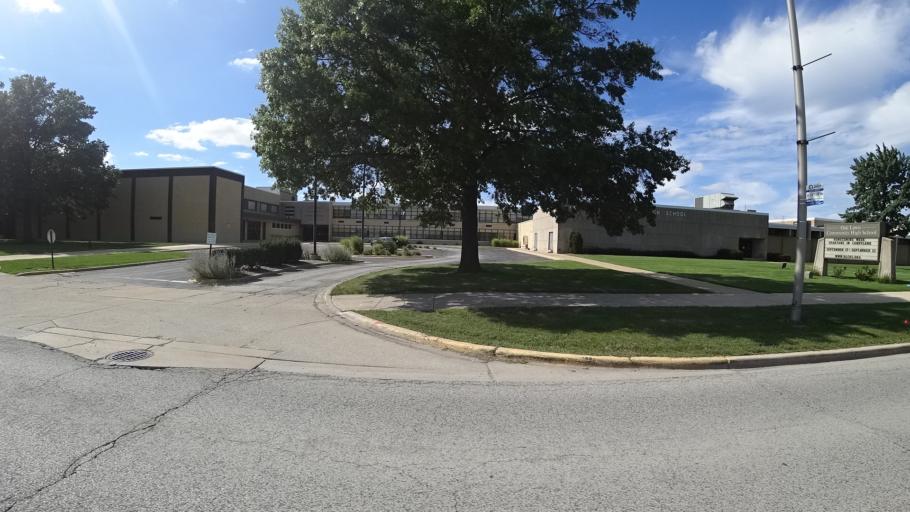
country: US
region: Illinois
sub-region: Cook County
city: Oak Lawn
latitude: 41.7212
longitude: -87.7672
